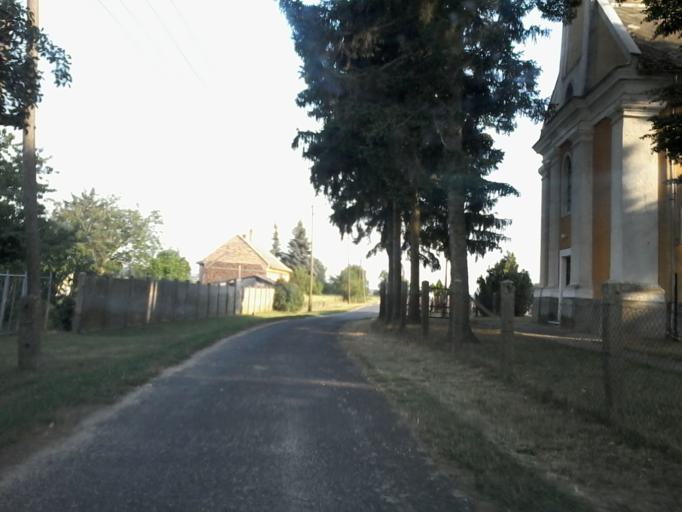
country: HU
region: Vas
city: Janoshaza
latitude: 47.1144
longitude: 17.2007
